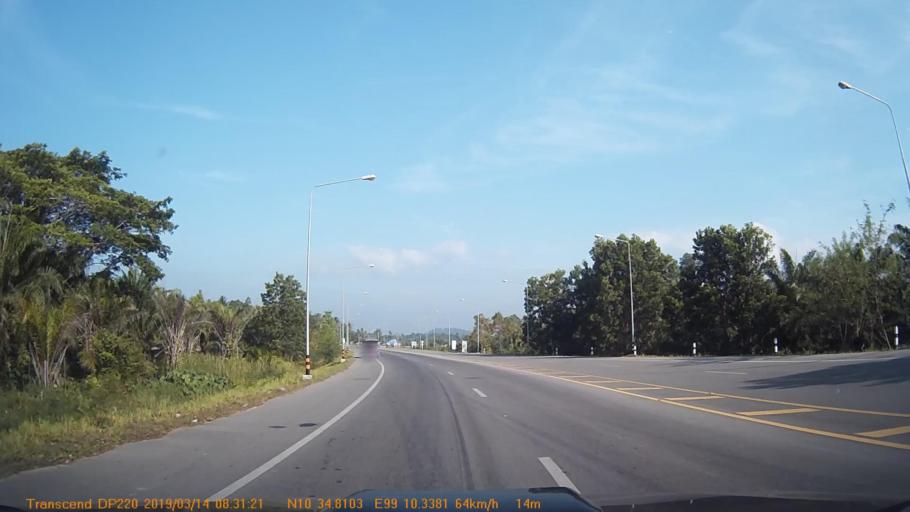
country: TH
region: Chumphon
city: Tha Sae
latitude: 10.5805
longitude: 99.1721
